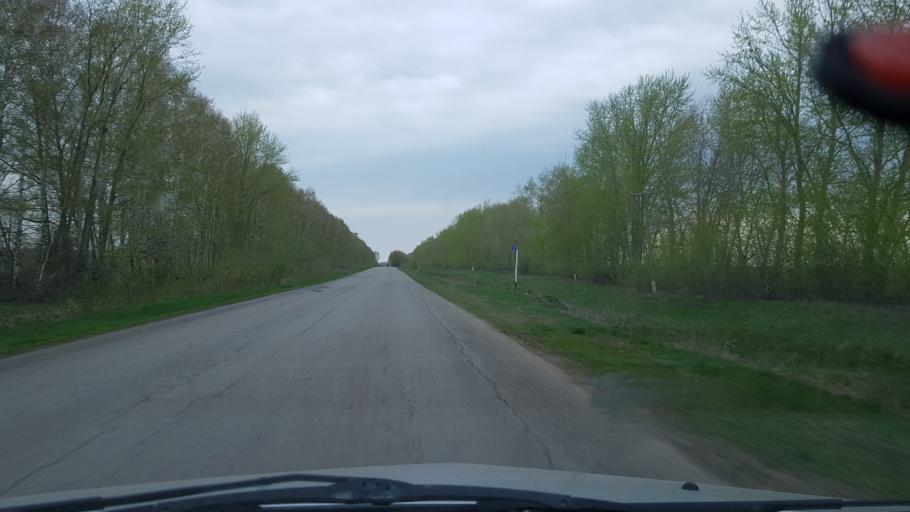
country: RU
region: Samara
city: Podstepki
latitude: 53.6642
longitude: 49.1831
